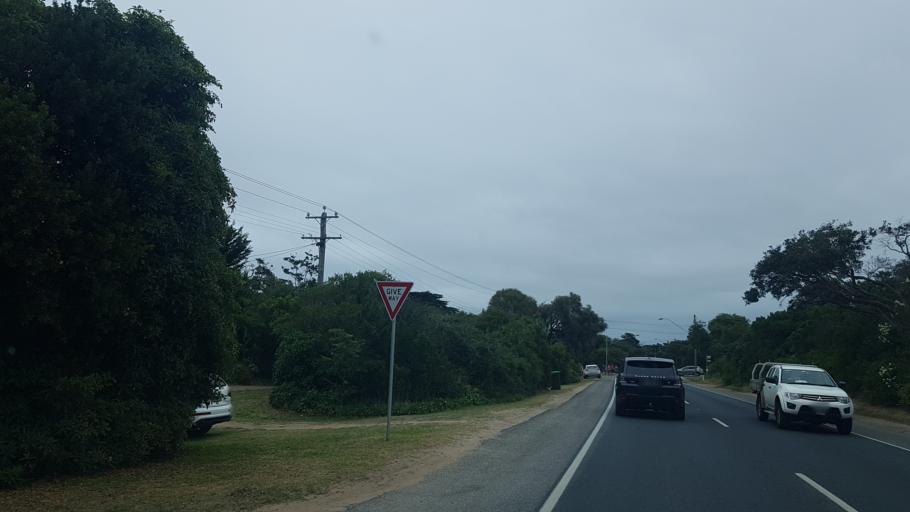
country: AU
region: Victoria
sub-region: Mornington Peninsula
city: Sorrento
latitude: -38.3486
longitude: 144.7434
